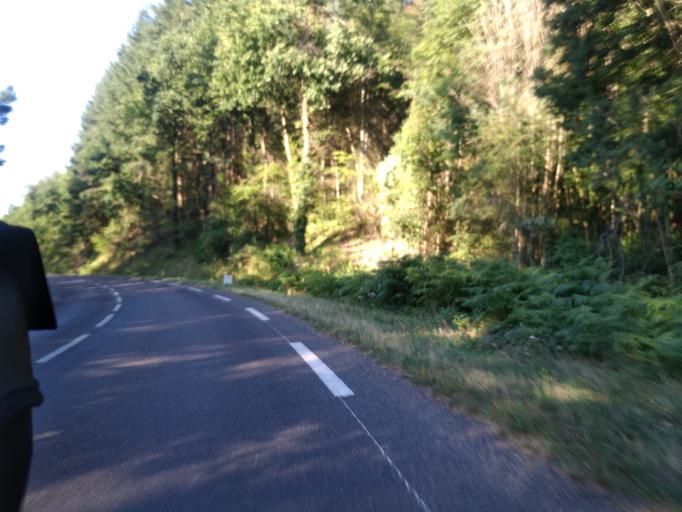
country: FR
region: Rhone-Alpes
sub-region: Departement de la Loire
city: Rozier-en-Donzy
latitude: 45.7435
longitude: 4.2986
